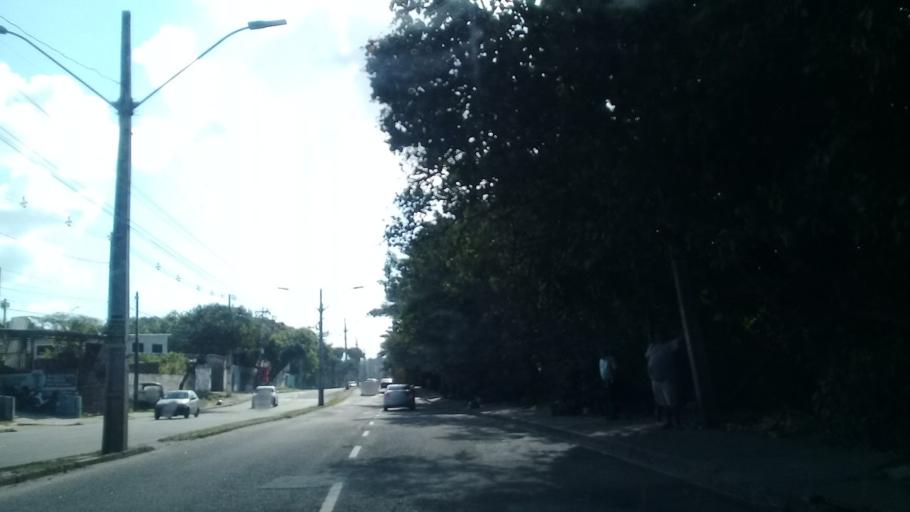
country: BR
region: Pernambuco
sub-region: Recife
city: Recife
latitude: -8.1077
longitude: -34.9312
